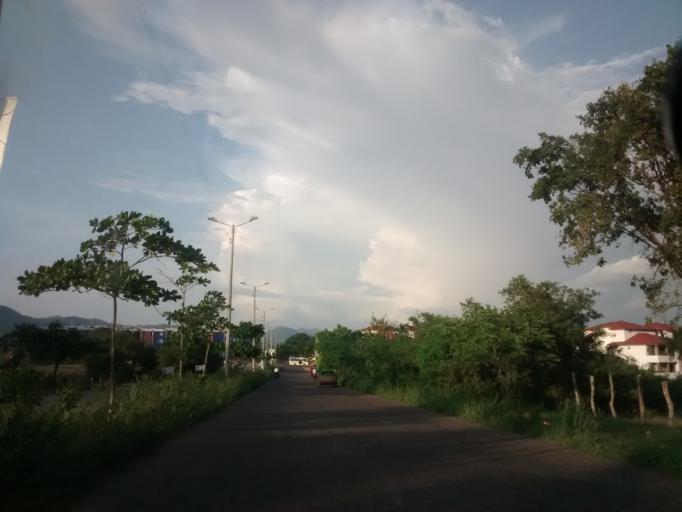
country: CO
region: Cundinamarca
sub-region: Girardot
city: Girardot City
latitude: 4.3189
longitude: -74.8066
